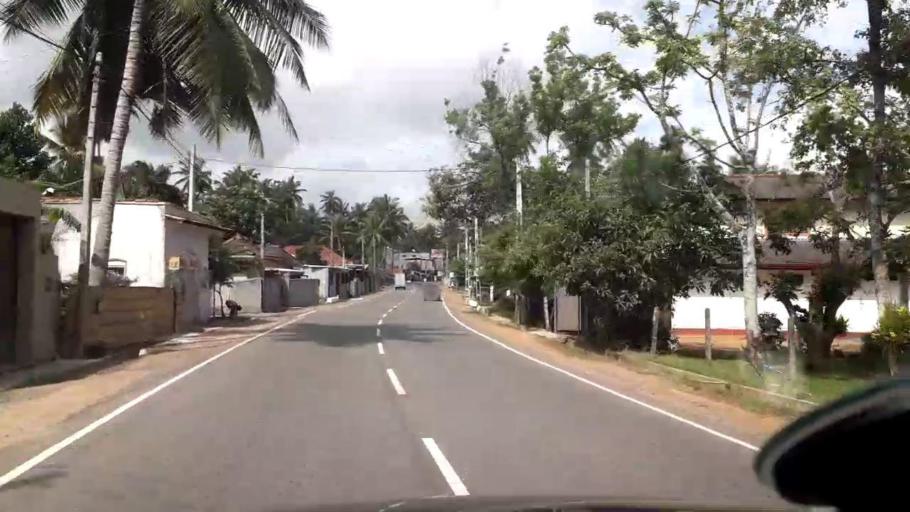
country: LK
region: Western
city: Panadura
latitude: 6.6699
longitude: 79.9396
